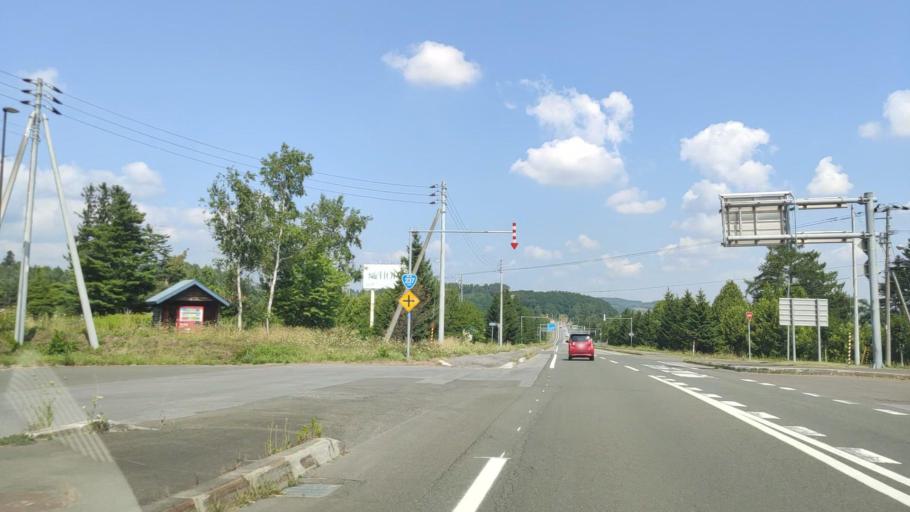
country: JP
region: Hokkaido
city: Shimo-furano
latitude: 43.4629
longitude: 142.4571
